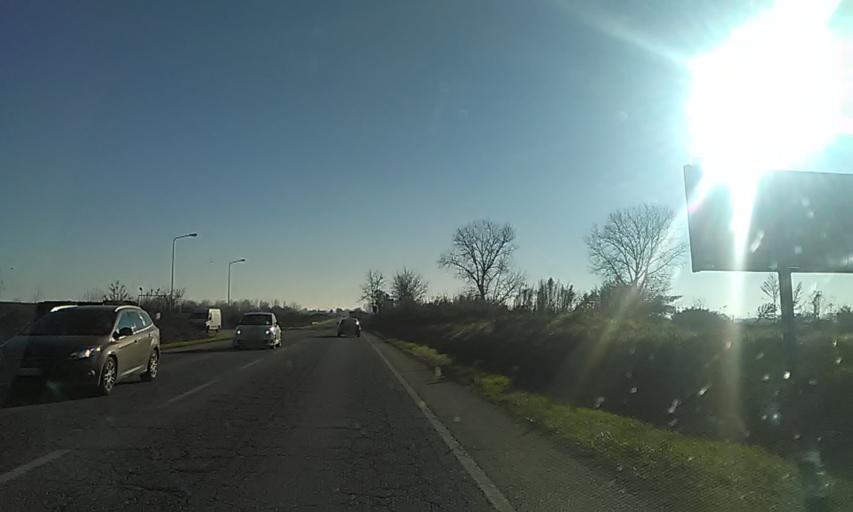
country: IT
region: Piedmont
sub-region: Provincia di Vercelli
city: Prarolo
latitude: 45.2699
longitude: 8.4638
